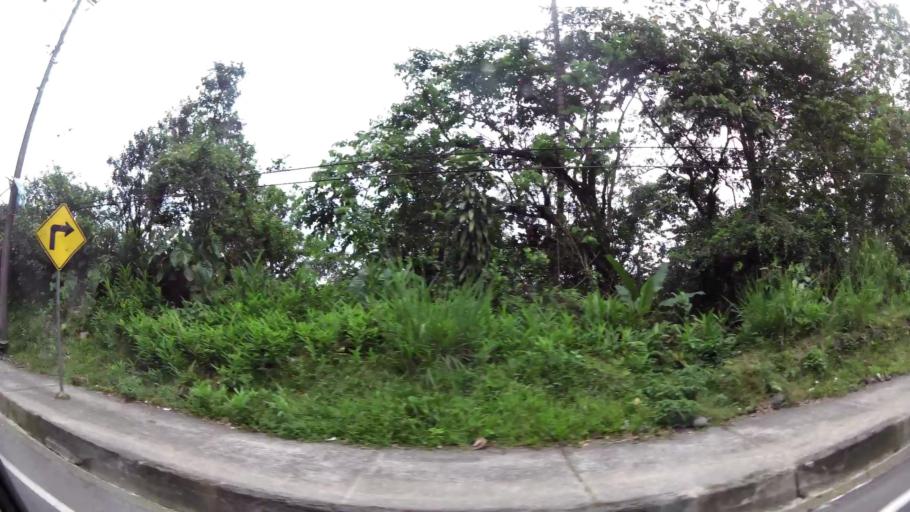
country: EC
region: Pastaza
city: Puyo
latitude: -1.5084
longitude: -78.0496
